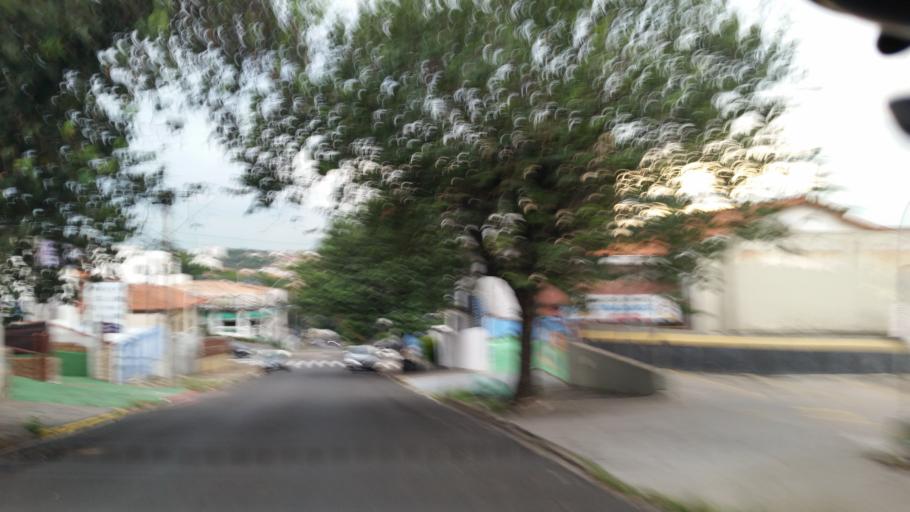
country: BR
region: Sao Paulo
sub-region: Campinas
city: Campinas
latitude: -22.9190
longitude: -47.0584
